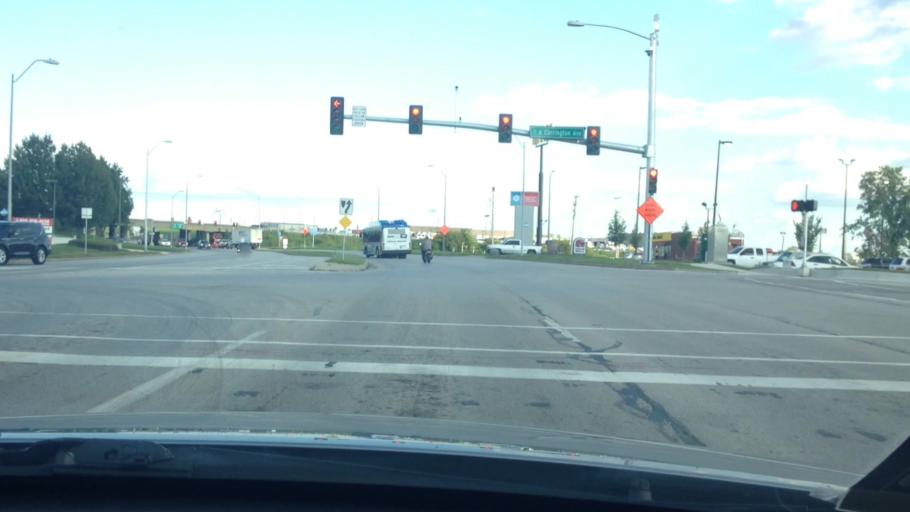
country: US
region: Missouri
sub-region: Clay County
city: Claycomo
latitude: 39.1687
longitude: -94.4966
